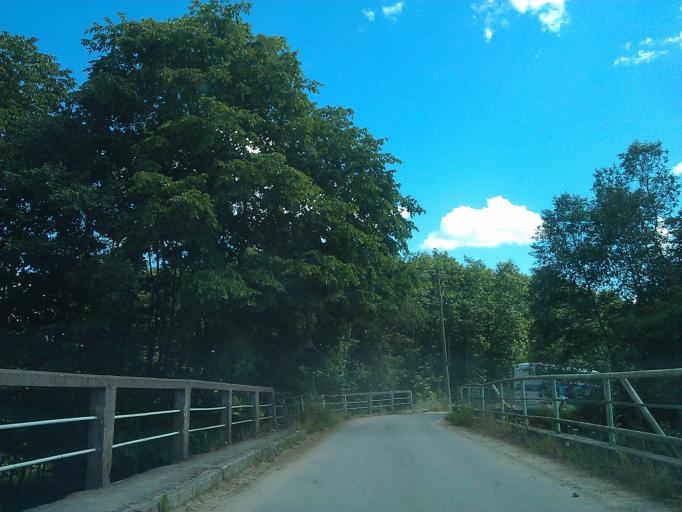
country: LV
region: Vilanu
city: Vilani
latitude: 56.5896
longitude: 26.9509
